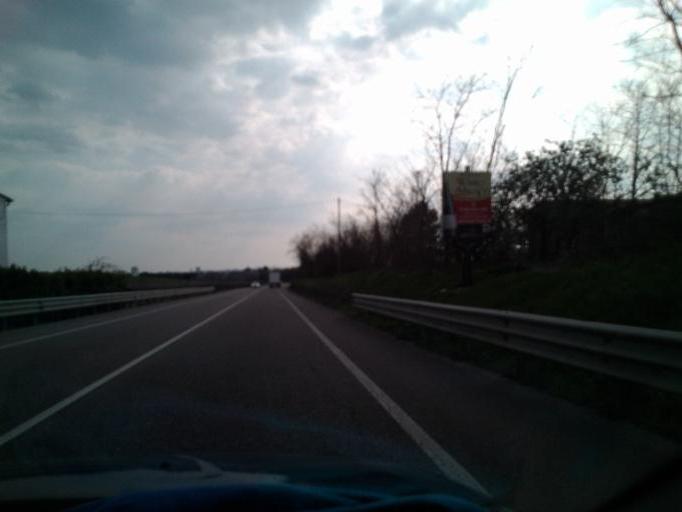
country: IT
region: Veneto
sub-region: Provincia di Verona
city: Pescantina
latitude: 45.5071
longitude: 10.8642
